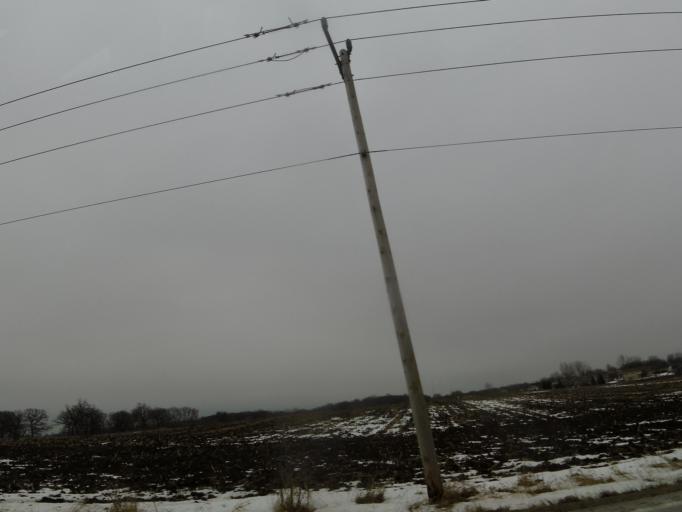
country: US
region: Minnesota
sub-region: Carver County
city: Cologne
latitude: 44.7809
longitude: -93.7881
